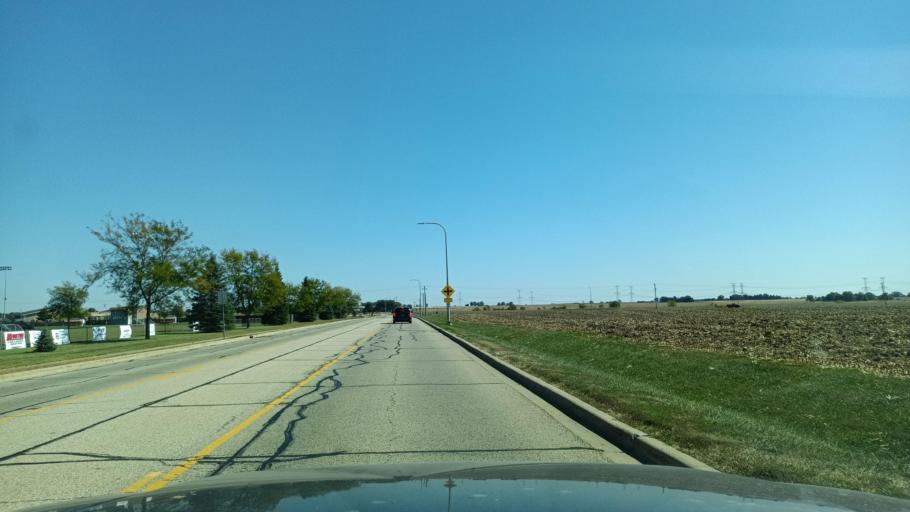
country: US
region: Illinois
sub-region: Tazewell County
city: Morton
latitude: 40.6133
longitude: -89.4349
